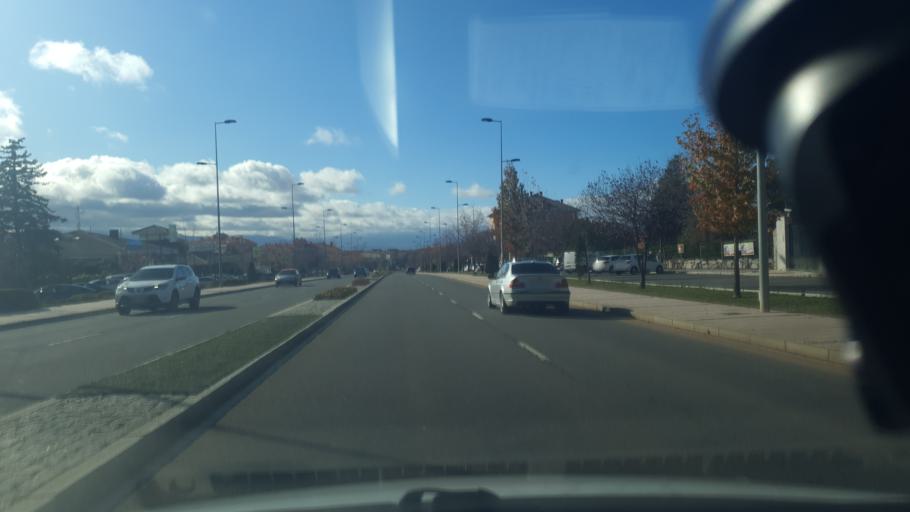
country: ES
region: Castille and Leon
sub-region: Provincia de Avila
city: Avila
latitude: 40.6632
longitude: -4.6703
